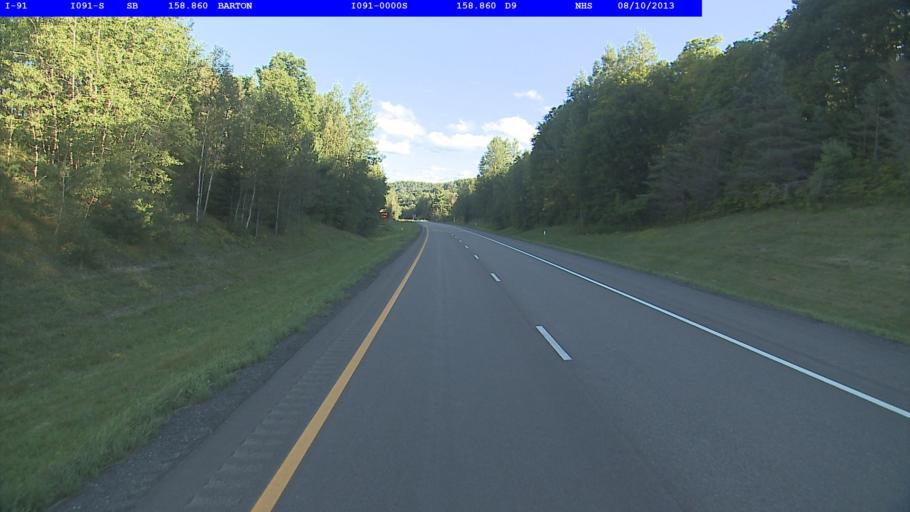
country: US
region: Vermont
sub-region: Orleans County
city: Newport
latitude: 44.7699
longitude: -72.2139
